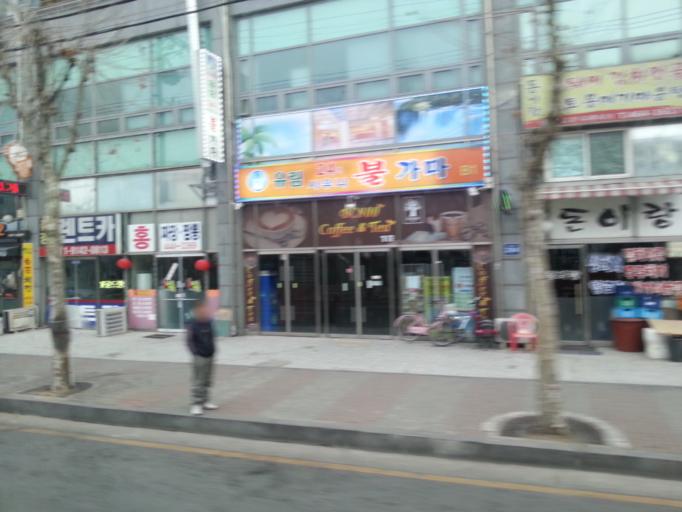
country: KR
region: Gyeonggi-do
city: Anyang-si
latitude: 37.4049
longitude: 126.9193
